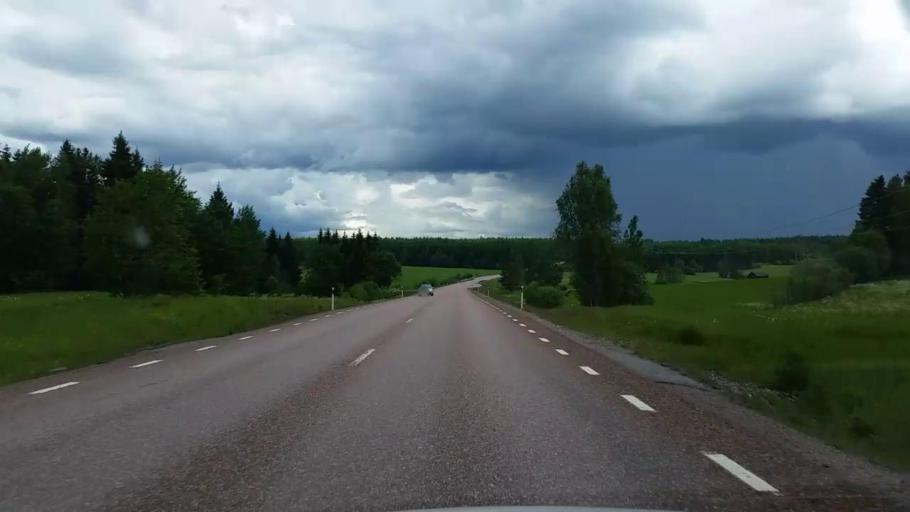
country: SE
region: Gaevleborg
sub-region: Hofors Kommun
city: Hofors
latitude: 60.5351
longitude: 16.4592
